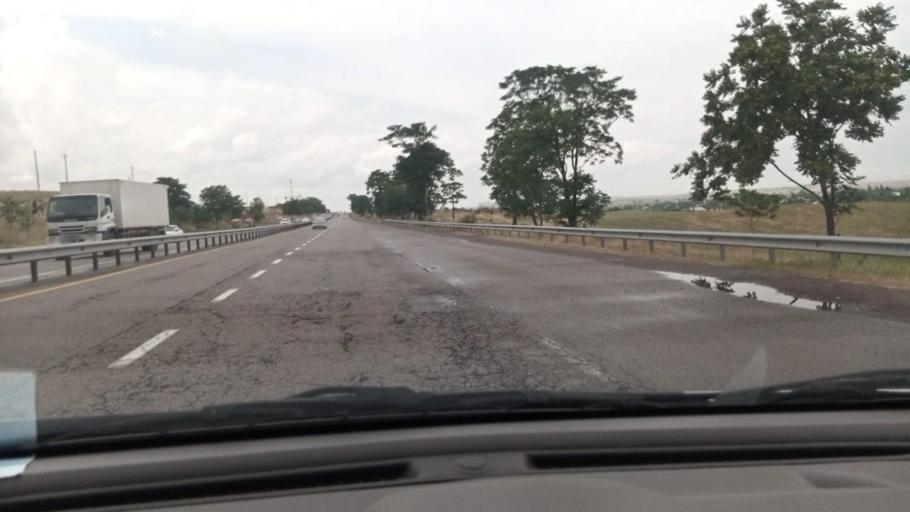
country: UZ
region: Toshkent
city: Ohangaron
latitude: 40.9769
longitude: 69.5432
